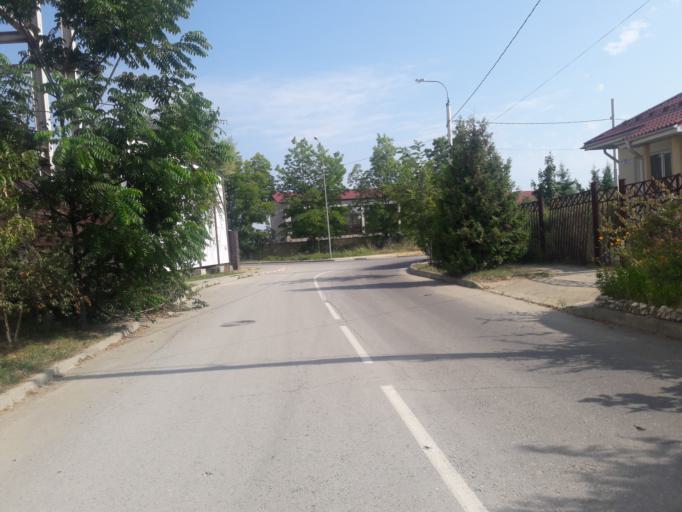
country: RU
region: Krasnodarskiy
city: Vysokoye
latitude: 43.3943
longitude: 40.0022
